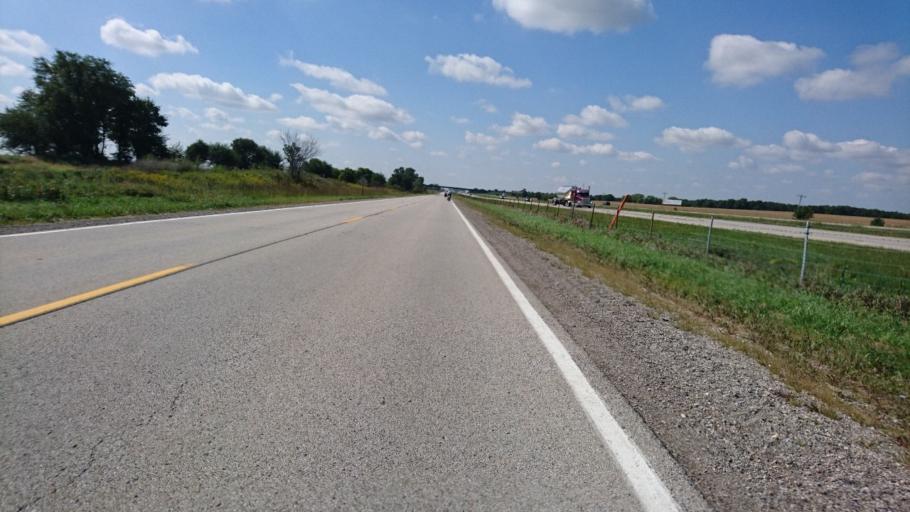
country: US
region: Illinois
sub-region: McLean County
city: Lexington
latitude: 40.6094
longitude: -88.8321
